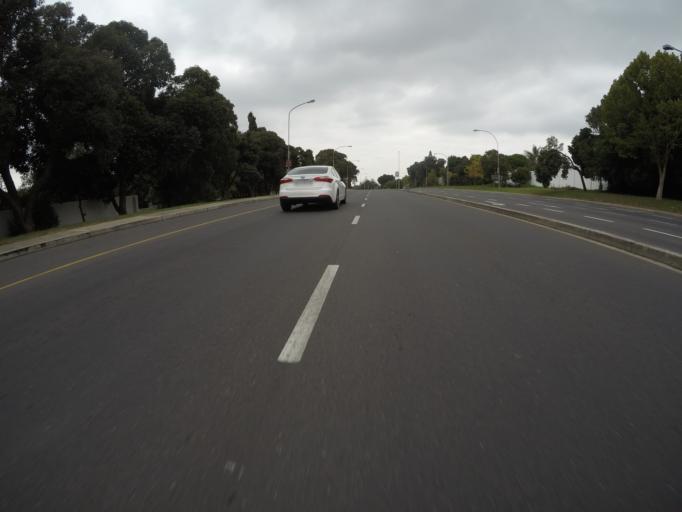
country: ZA
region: Western Cape
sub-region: City of Cape Town
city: Kraaifontein
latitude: -33.8534
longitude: 18.6438
